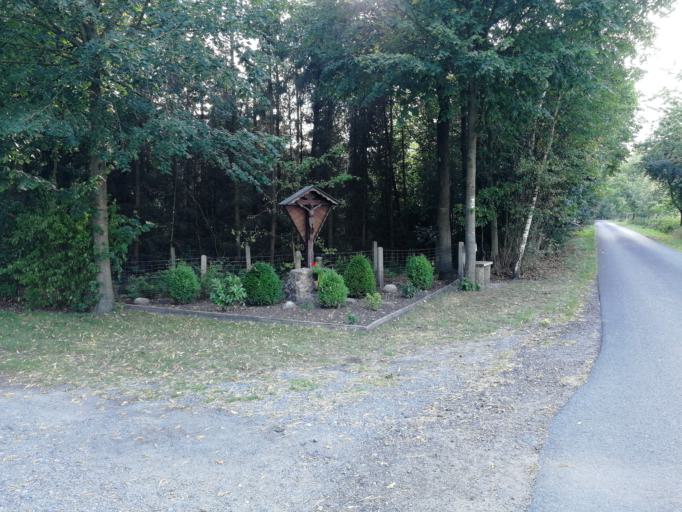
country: DE
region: Lower Saxony
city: Salzbergen
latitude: 52.3018
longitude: 7.3150
